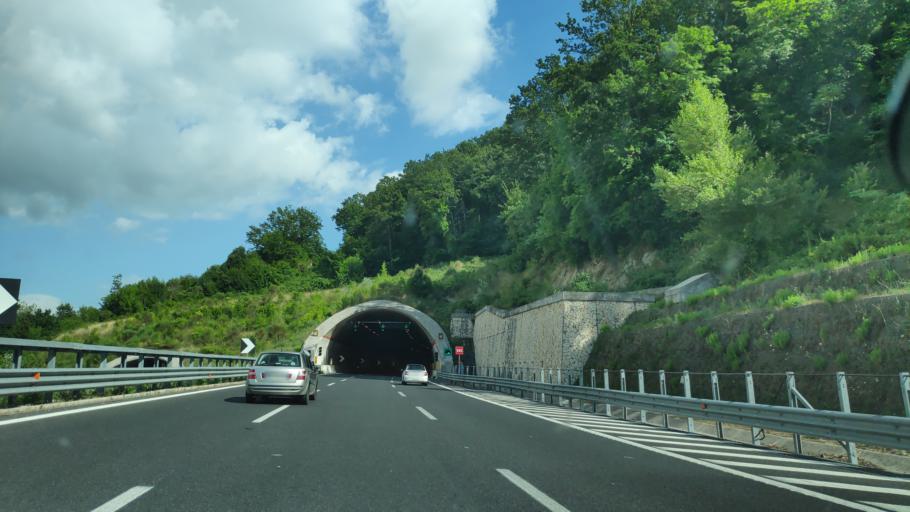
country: IT
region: Campania
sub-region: Provincia di Salerno
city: Contursi Terme
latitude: 40.6268
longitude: 15.2366
